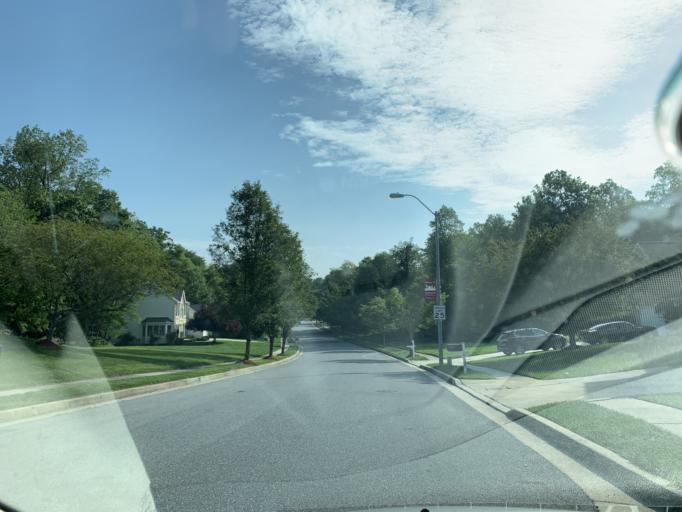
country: US
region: Maryland
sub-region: Baltimore County
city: Randallstown
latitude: 39.3895
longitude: -76.7974
